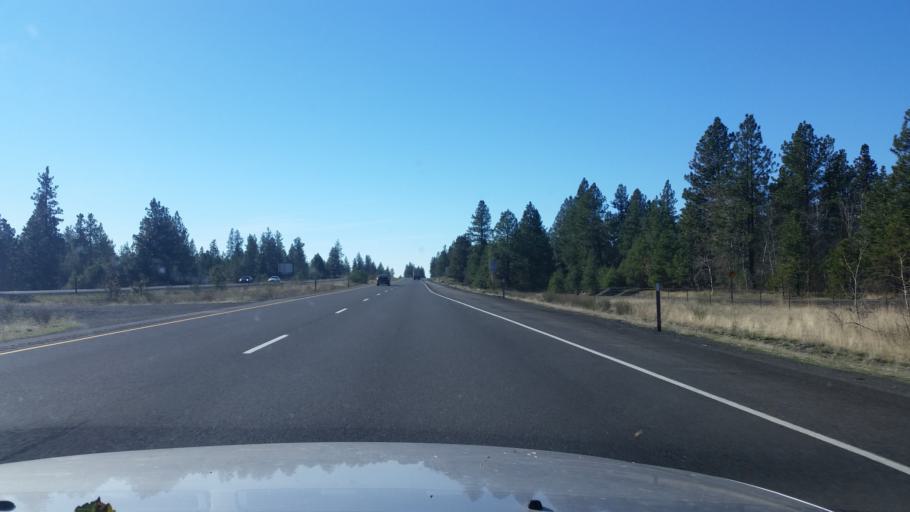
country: US
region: Washington
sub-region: Spokane County
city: Medical Lake
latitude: 47.4322
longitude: -117.7959
